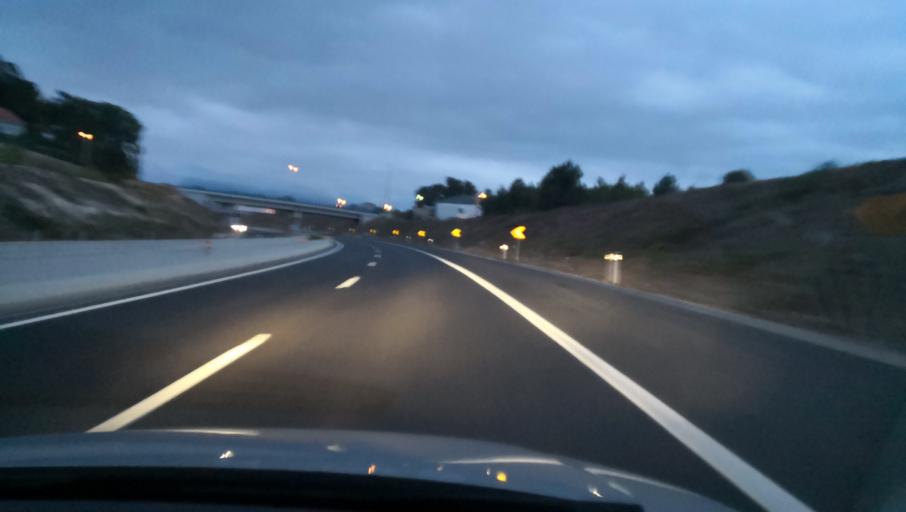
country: PT
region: Setubal
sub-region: Seixal
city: Arrentela
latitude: 38.5936
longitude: -9.0998
